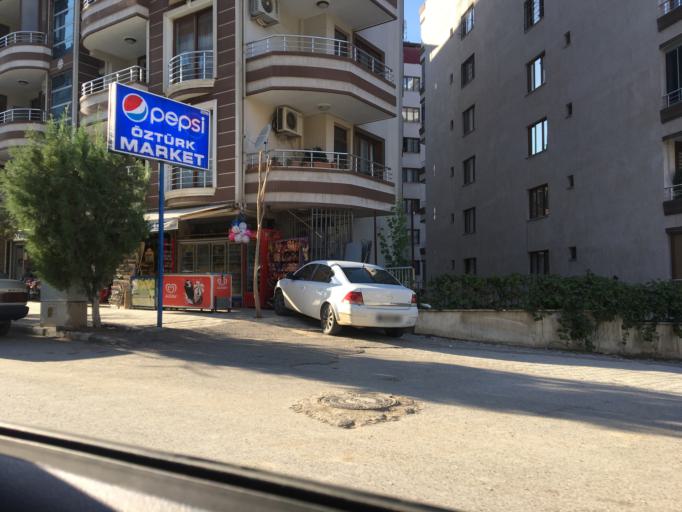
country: TR
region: Hatay
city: Kirikhan
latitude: 36.4933
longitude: 36.3422
